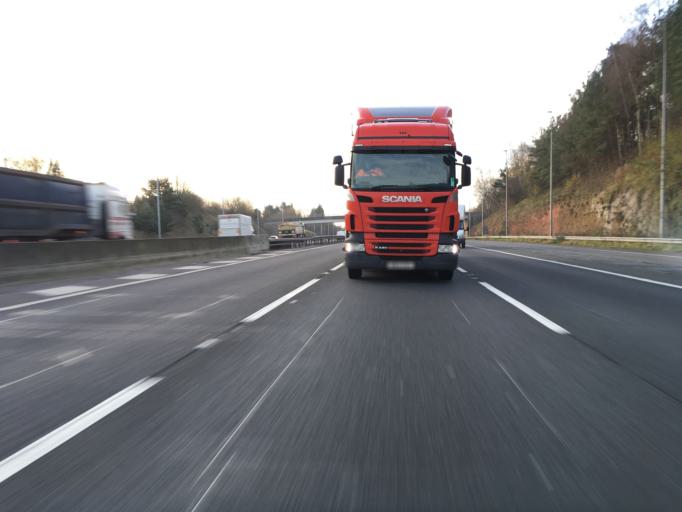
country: GB
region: England
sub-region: Worcestershire
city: Bromsgrove
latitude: 52.3610
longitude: -2.0691
